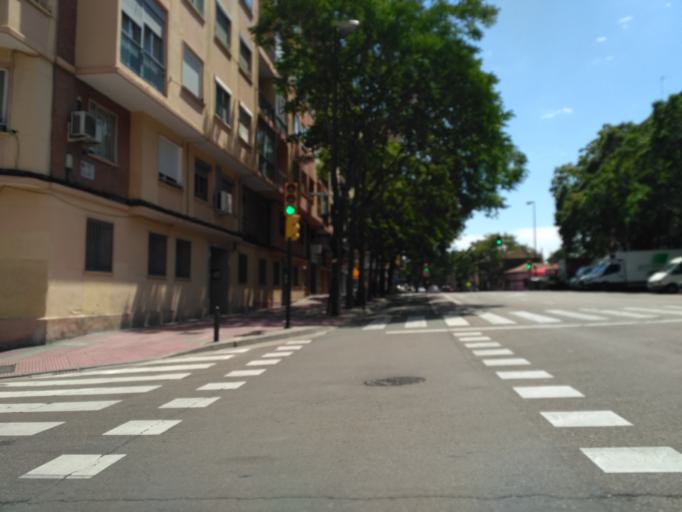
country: ES
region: Aragon
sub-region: Provincia de Zaragoza
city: Delicias
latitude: 41.6491
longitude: -0.9024
